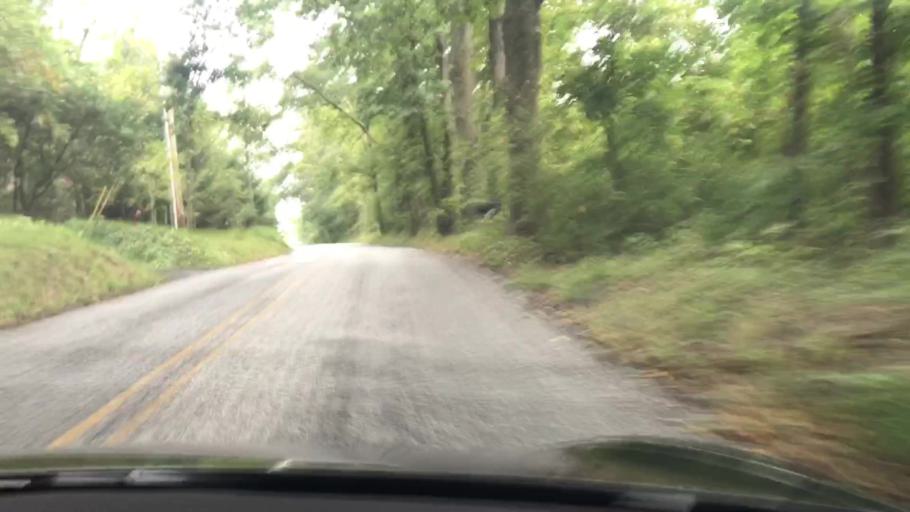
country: US
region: Pennsylvania
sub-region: York County
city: Dillsburg
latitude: 40.1119
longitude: -76.9680
